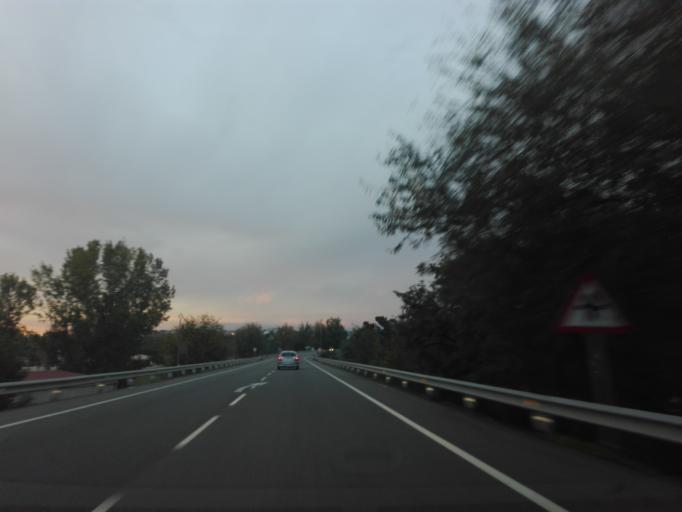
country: ES
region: Extremadura
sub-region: Provincia de Caceres
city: Coria
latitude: 39.9746
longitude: -6.5256
